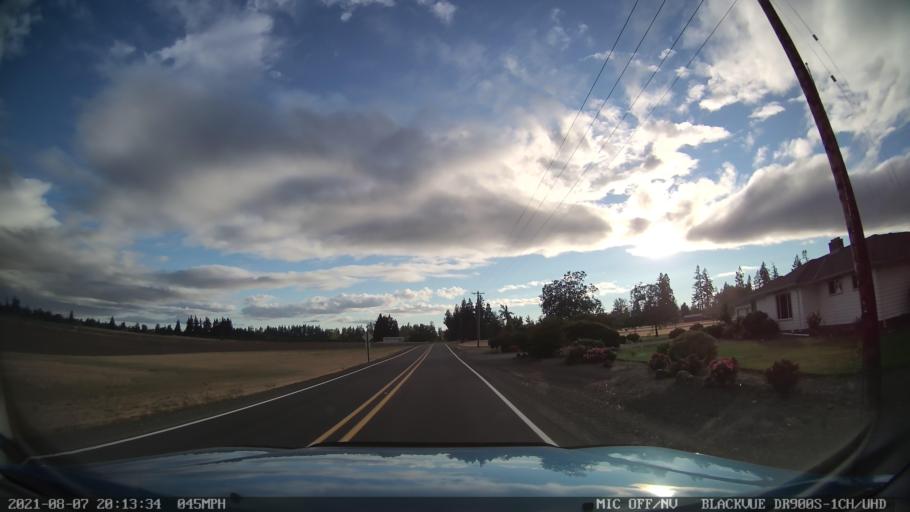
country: US
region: Oregon
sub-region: Marion County
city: Hayesville
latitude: 44.9569
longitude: -122.9257
